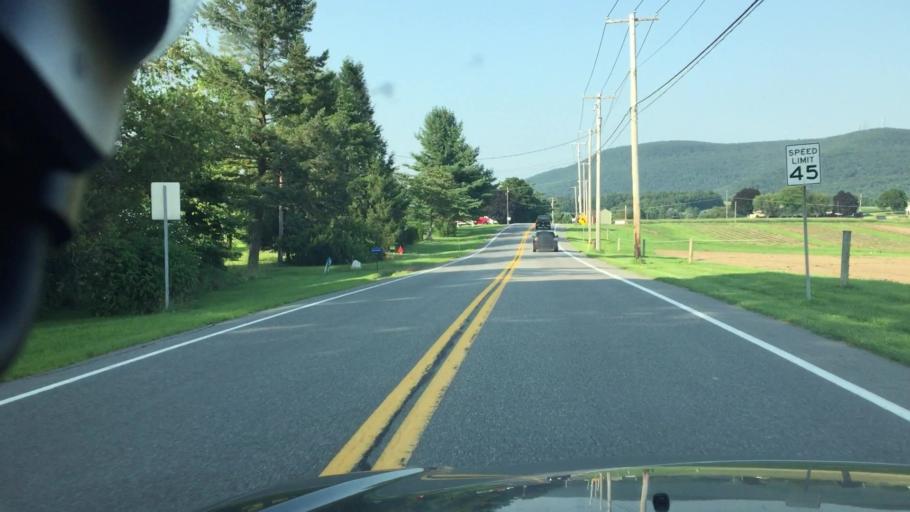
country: US
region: Pennsylvania
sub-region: Columbia County
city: Catawissa
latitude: 40.9249
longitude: -76.4627
